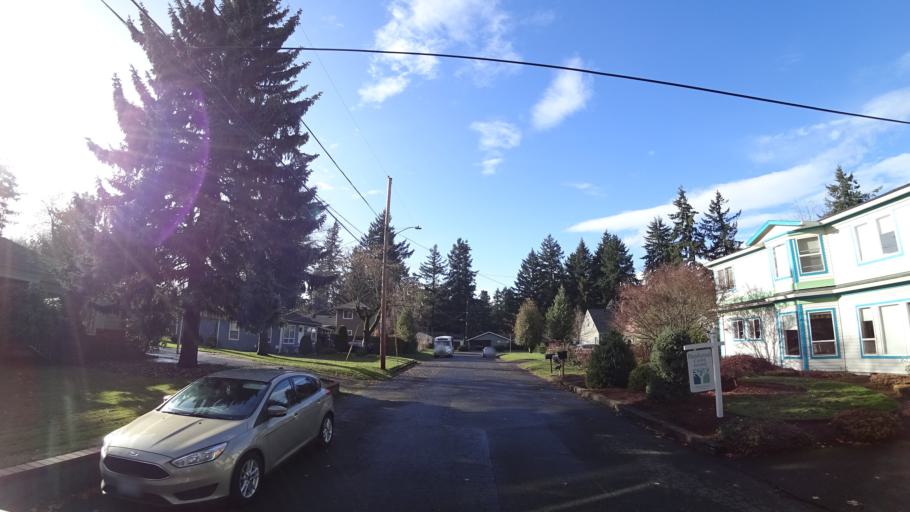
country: US
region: Oregon
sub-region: Multnomah County
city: Lents
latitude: 45.5290
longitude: -122.5438
